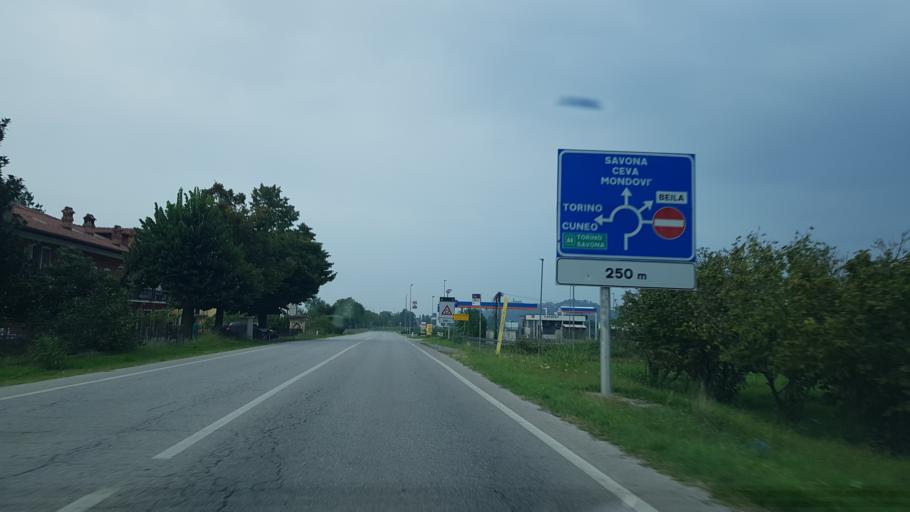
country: IT
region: Piedmont
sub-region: Provincia di Cuneo
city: Villanova Mondovi
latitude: 44.3655
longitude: 7.7960
